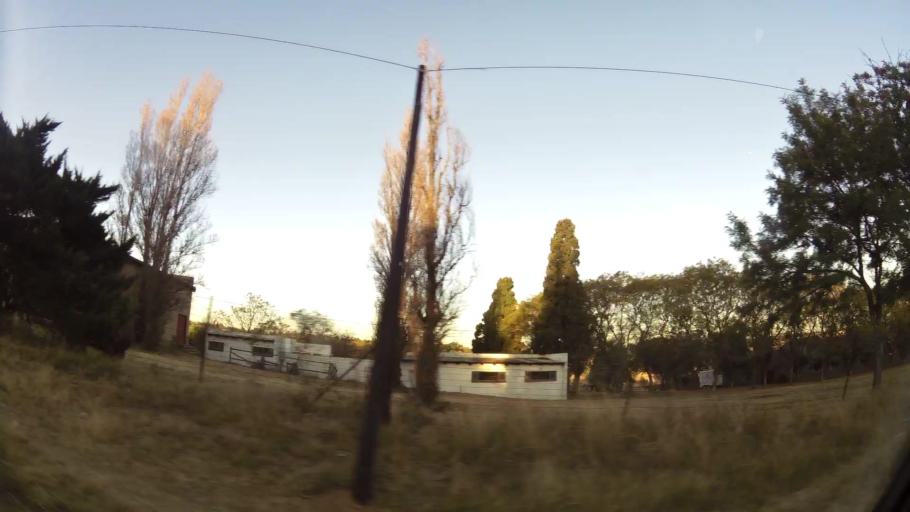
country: ZA
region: Gauteng
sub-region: City of Johannesburg Metropolitan Municipality
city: Diepsloot
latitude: -25.9458
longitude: 28.0531
